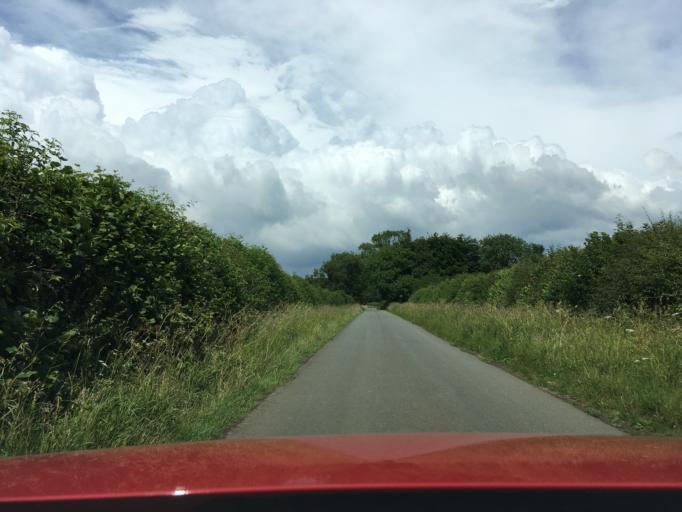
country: GB
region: England
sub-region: Gloucestershire
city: Chalford
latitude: 51.6912
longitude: -2.1281
